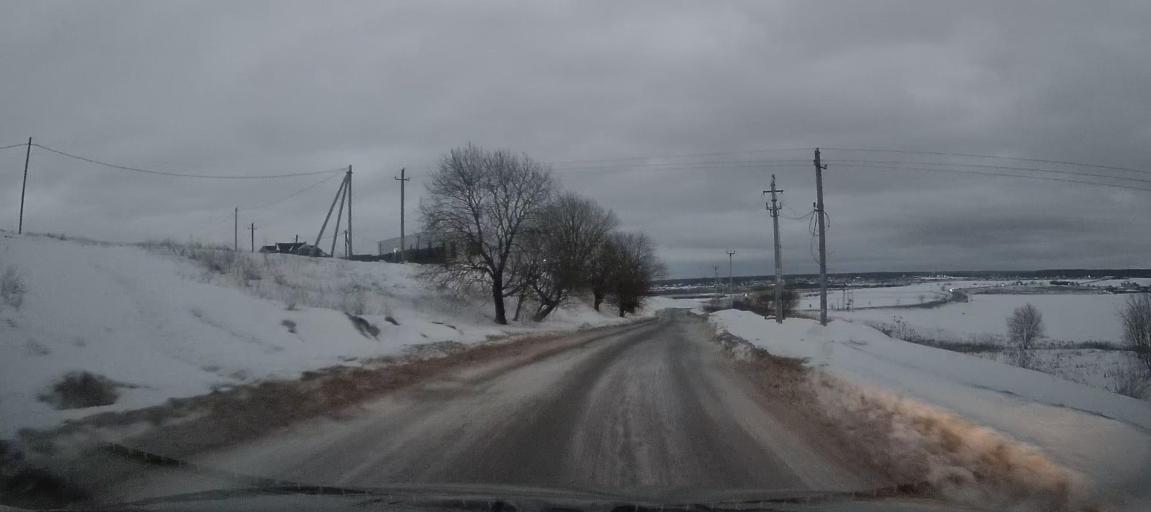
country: RU
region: Leningrad
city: Taytsy
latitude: 59.6940
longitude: 30.1461
